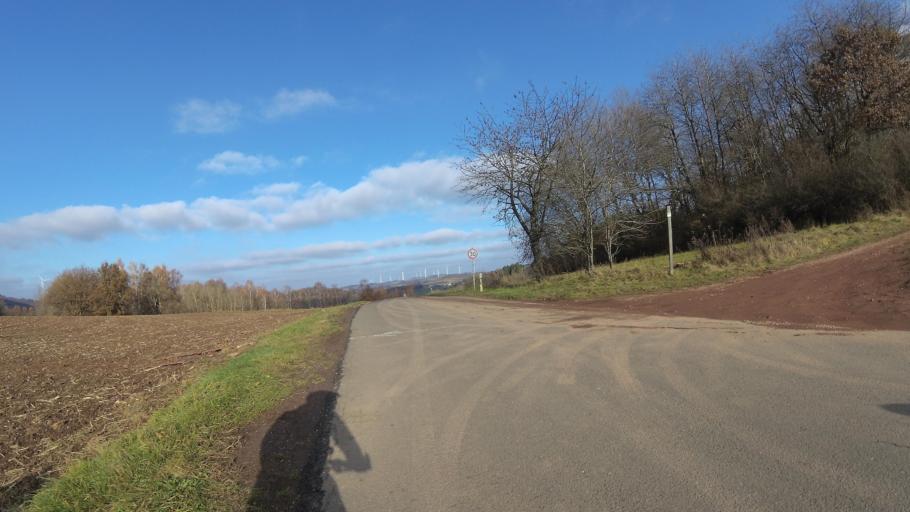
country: DE
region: Rheinland-Pfalz
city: Hahnweiler
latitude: 49.5233
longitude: 7.1875
